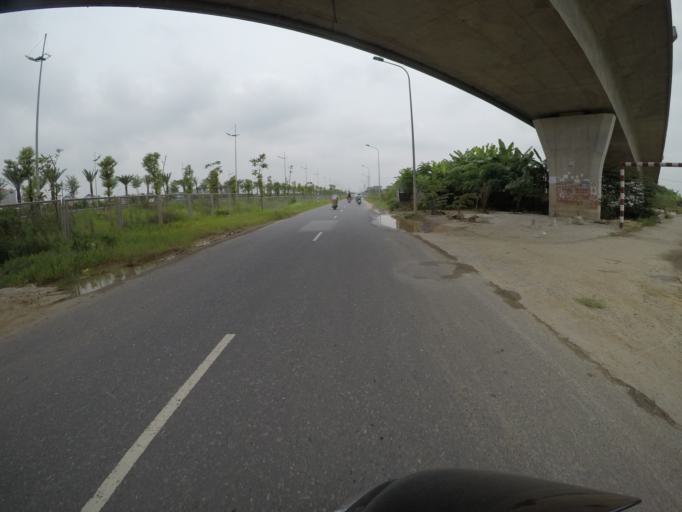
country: VN
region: Ha Noi
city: Dong Anh
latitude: 21.1749
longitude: 105.8249
